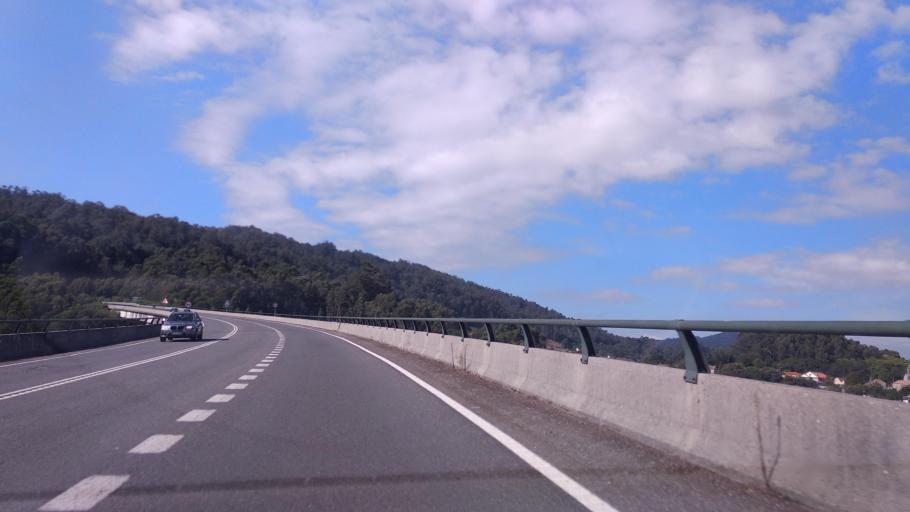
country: ES
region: Galicia
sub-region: Provincia de Pontevedra
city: Moana
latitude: 42.2816
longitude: -8.7521
